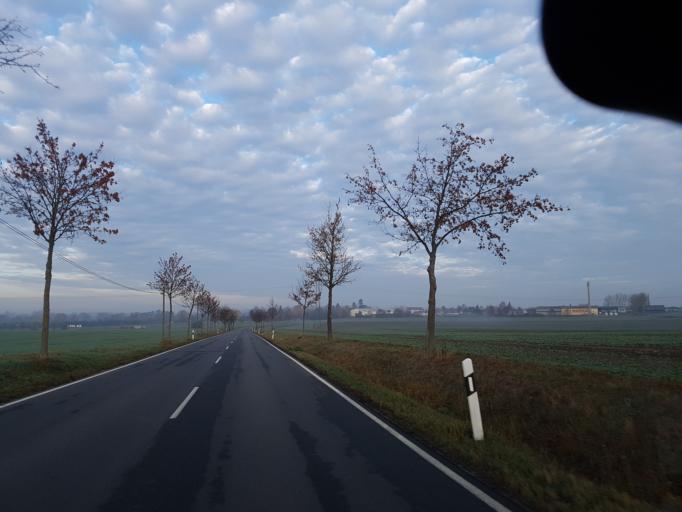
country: DE
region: Saxony-Anhalt
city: Zahna
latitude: 51.9071
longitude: 12.8080
